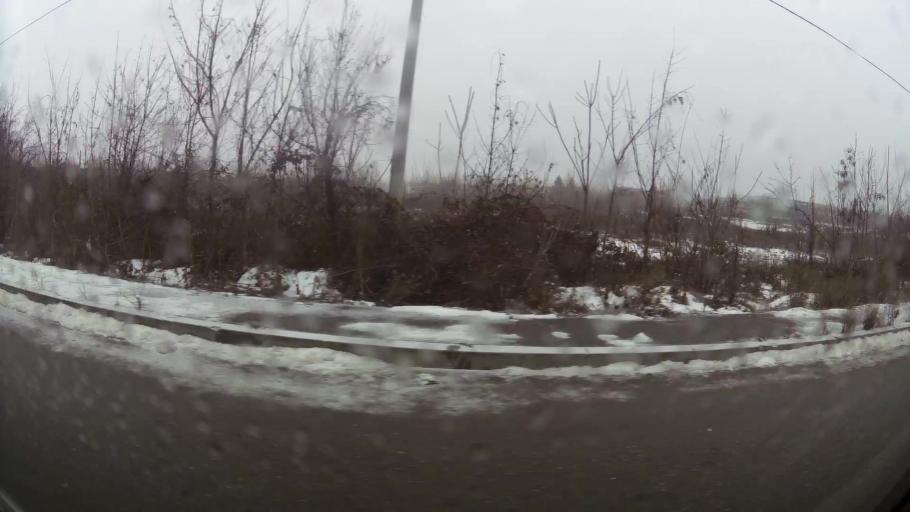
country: RO
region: Prahova
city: Ploiesti
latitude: 44.9529
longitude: 26.0318
